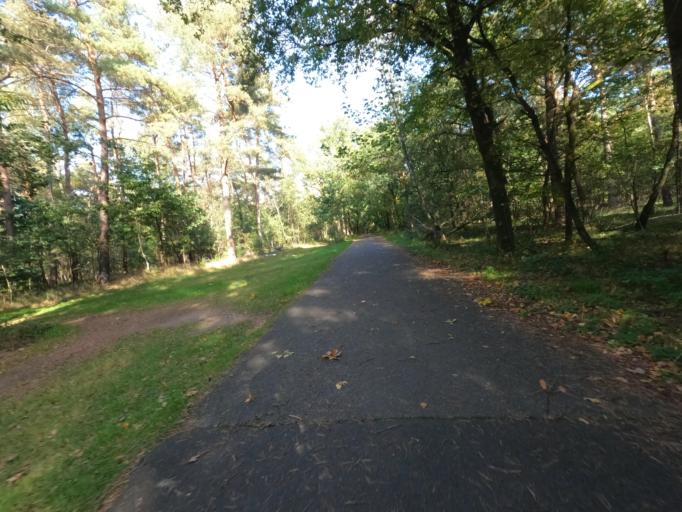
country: DE
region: North Rhine-Westphalia
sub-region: Regierungsbezirk Koln
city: Wassenberg
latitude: 51.1235
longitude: 6.1699
